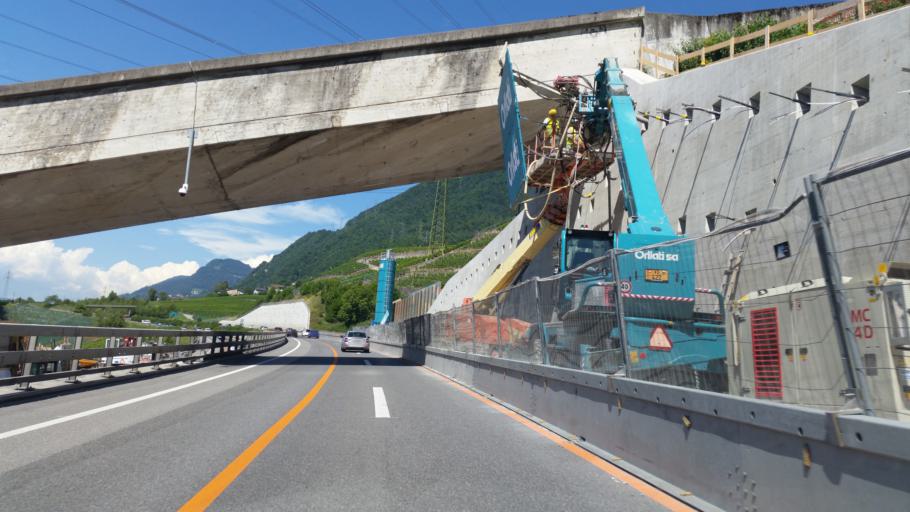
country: CH
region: Vaud
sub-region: Aigle District
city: Villeneuve
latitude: 46.3932
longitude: 6.9378
